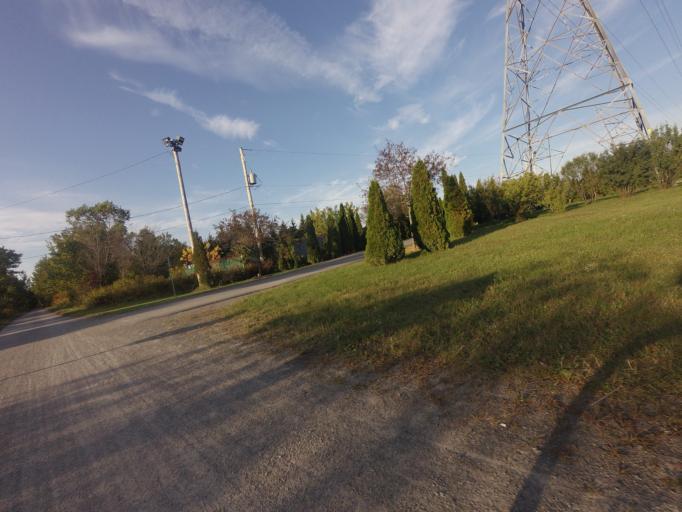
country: CA
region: Quebec
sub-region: Laurentides
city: Prevost
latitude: 45.8228
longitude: -74.0522
